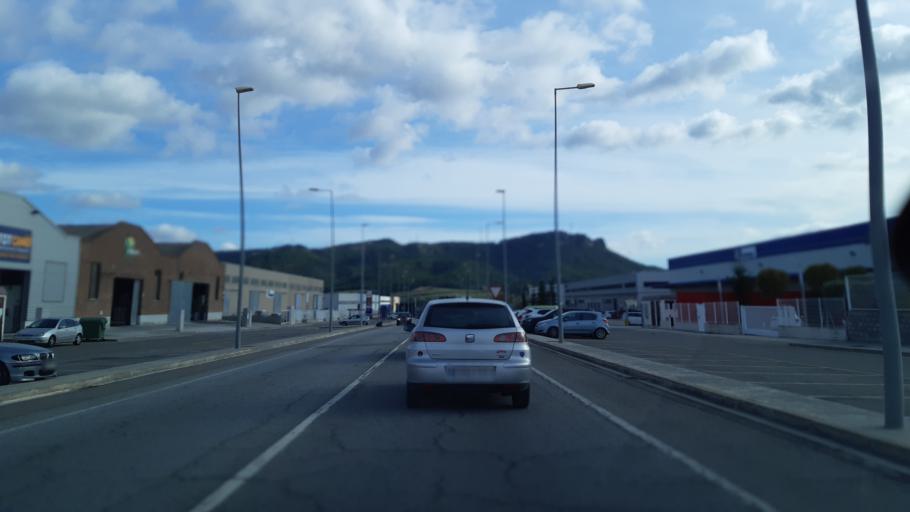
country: ES
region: Catalonia
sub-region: Provincia de Barcelona
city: Vilanova del Cami
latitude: 41.5773
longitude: 1.6542
